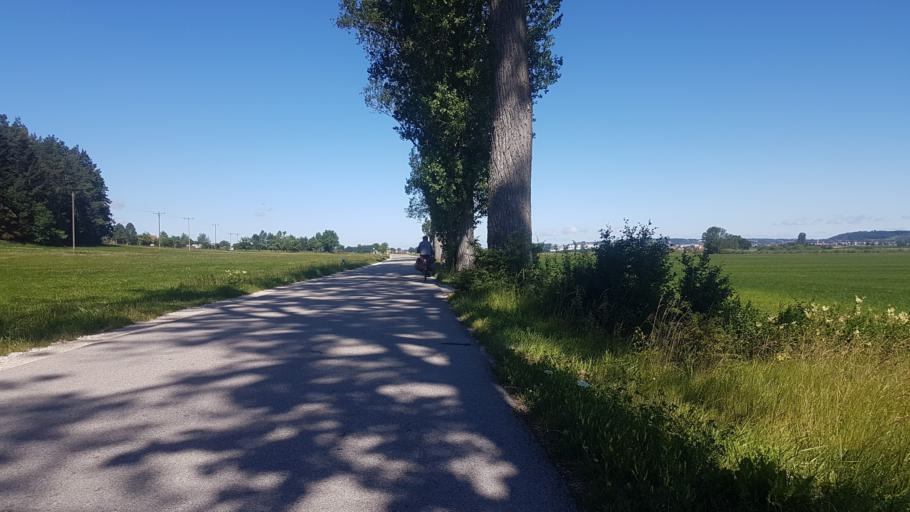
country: DE
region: Bavaria
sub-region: Regierungsbezirk Mittelfranken
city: Herrieden
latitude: 49.2082
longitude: 10.5402
